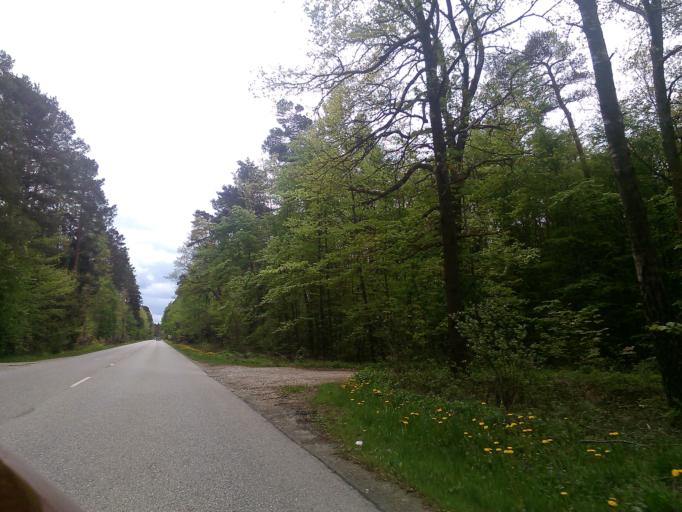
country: DE
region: Bavaria
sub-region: Upper Bavaria
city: Krailling
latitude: 48.1051
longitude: 11.3742
